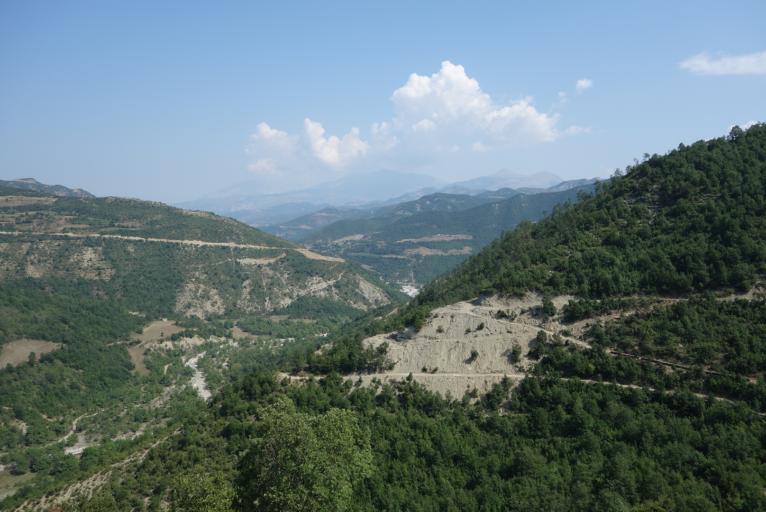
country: AL
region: Berat
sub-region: Rrethi i Skraparit
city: Cepan
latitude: 40.4065
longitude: 20.2997
